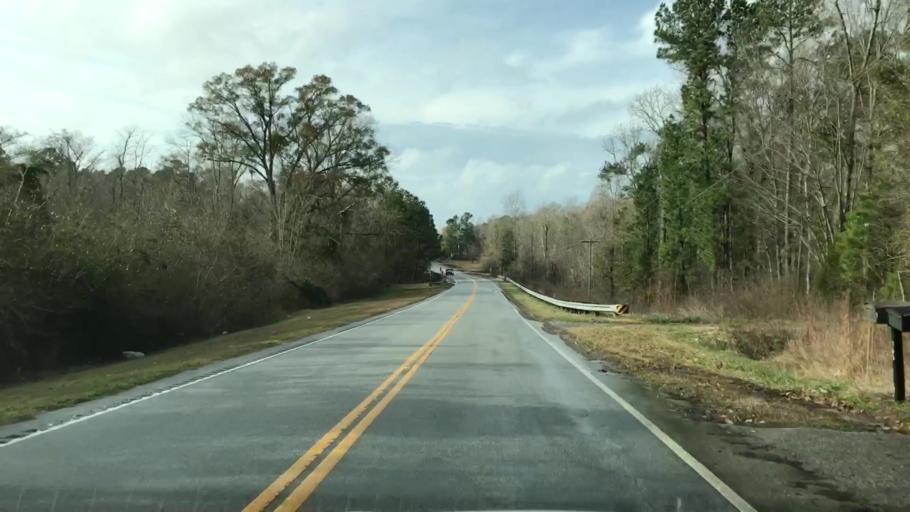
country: US
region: South Carolina
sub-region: Williamsburg County
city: Andrews
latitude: 33.4987
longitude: -79.5125
